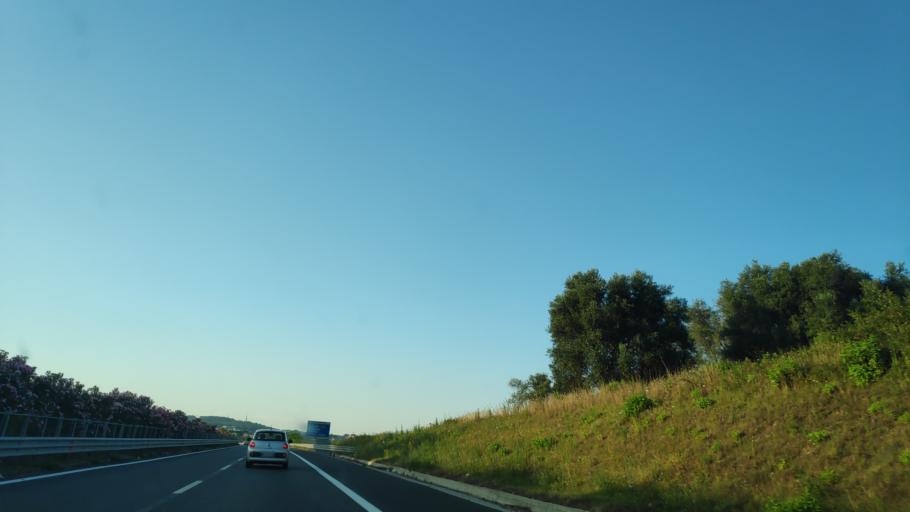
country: IT
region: Calabria
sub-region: Provincia di Reggio Calabria
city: Ceramida-Pellegrina
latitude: 38.3045
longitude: 15.8441
